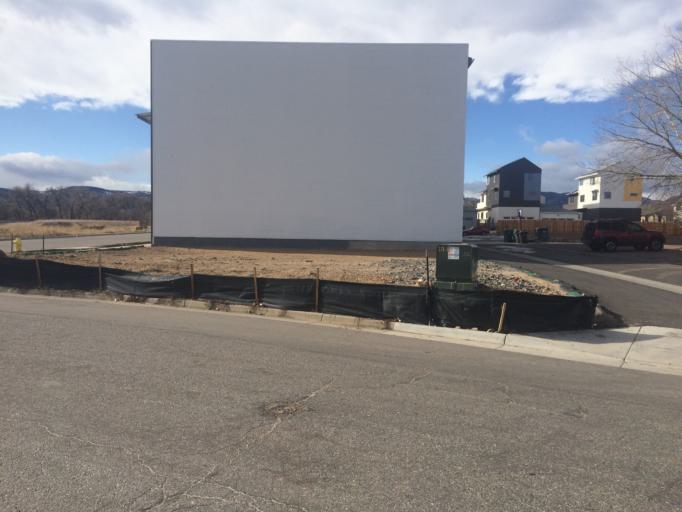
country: US
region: Colorado
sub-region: Jefferson County
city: Applewood
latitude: 39.8224
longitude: -105.1690
